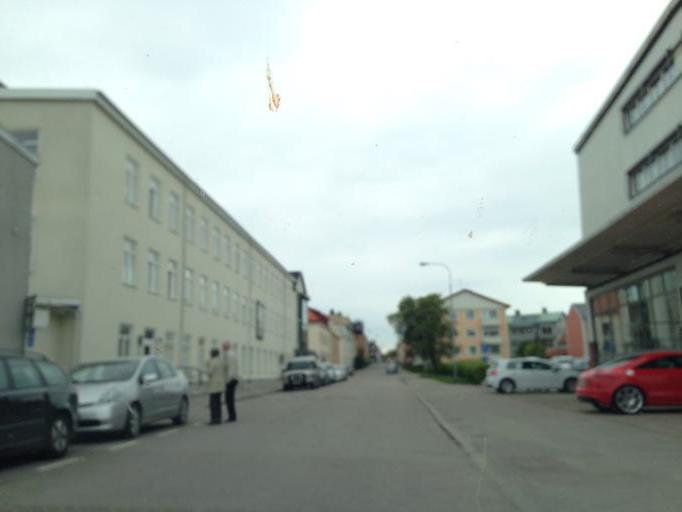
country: SE
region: Soedermanland
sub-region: Nykopings Kommun
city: Nykoping
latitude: 58.7480
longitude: 17.0069
